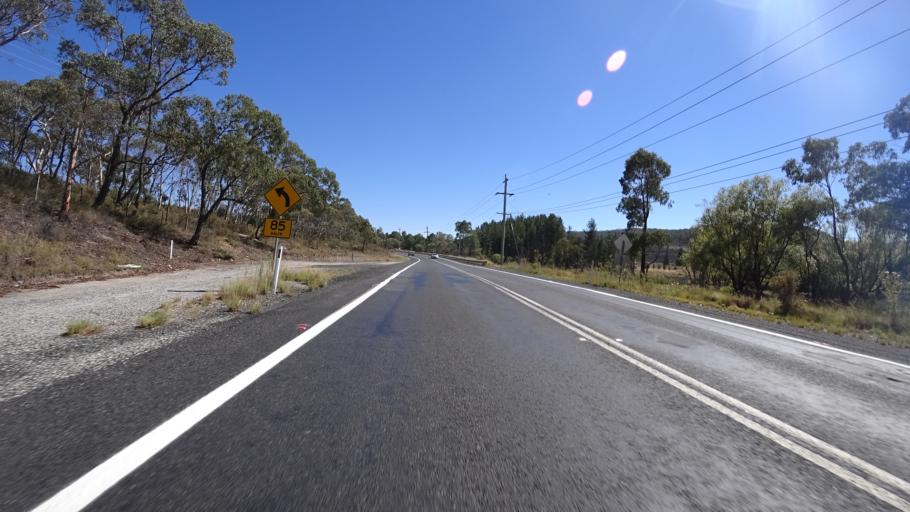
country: AU
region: New South Wales
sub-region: Lithgow
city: Portland
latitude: -33.3618
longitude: 150.0577
